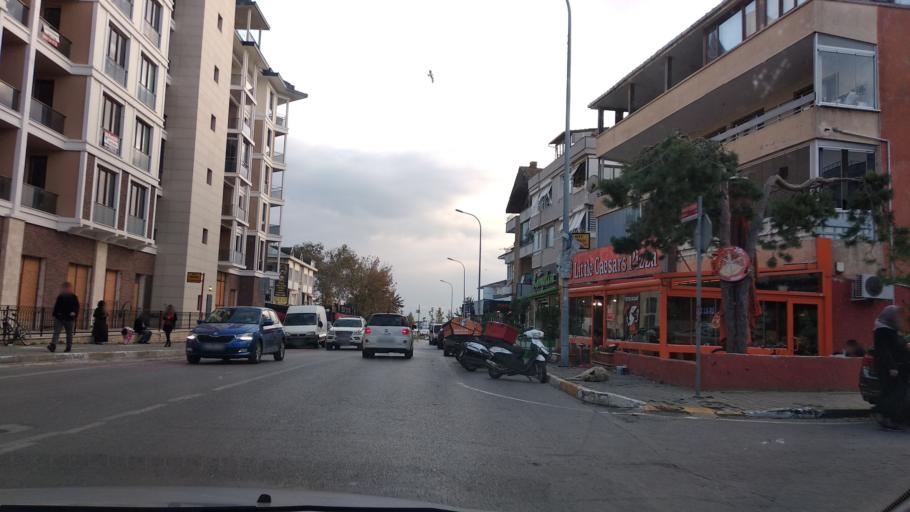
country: TR
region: Istanbul
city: Icmeler
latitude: 40.8183
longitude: 29.2984
